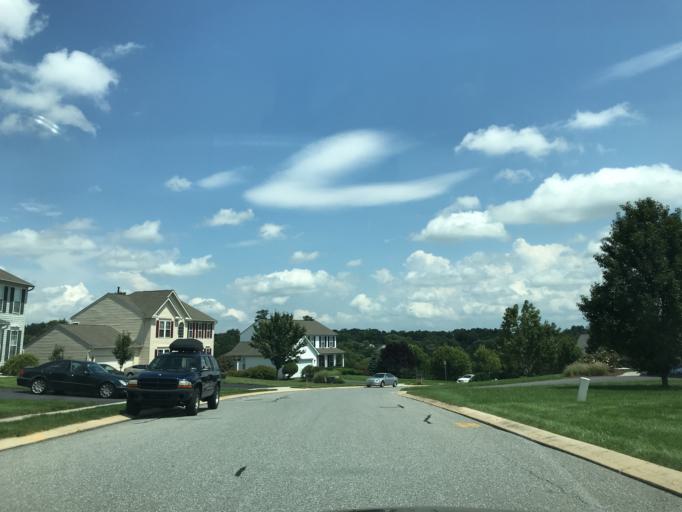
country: US
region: Pennsylvania
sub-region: York County
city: New Freedom
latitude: 39.7242
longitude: -76.7024
